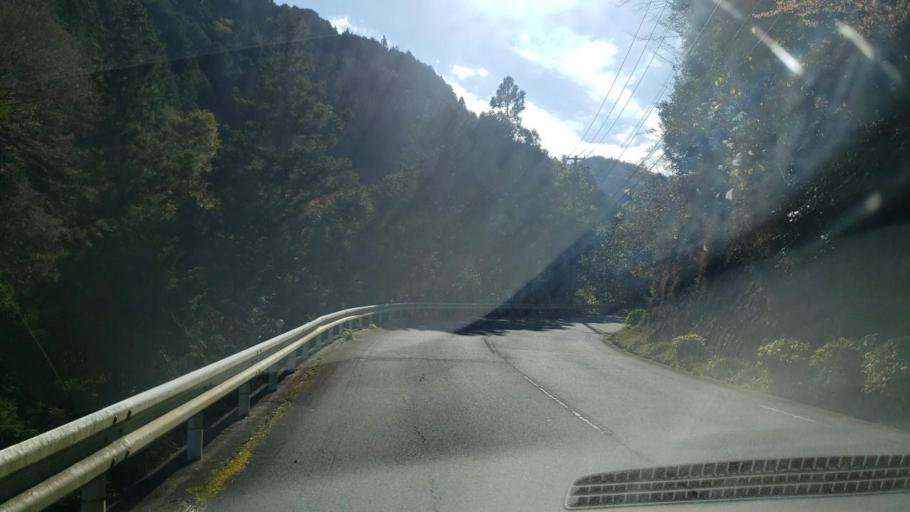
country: JP
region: Tokushima
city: Wakimachi
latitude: 34.0173
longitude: 134.0351
